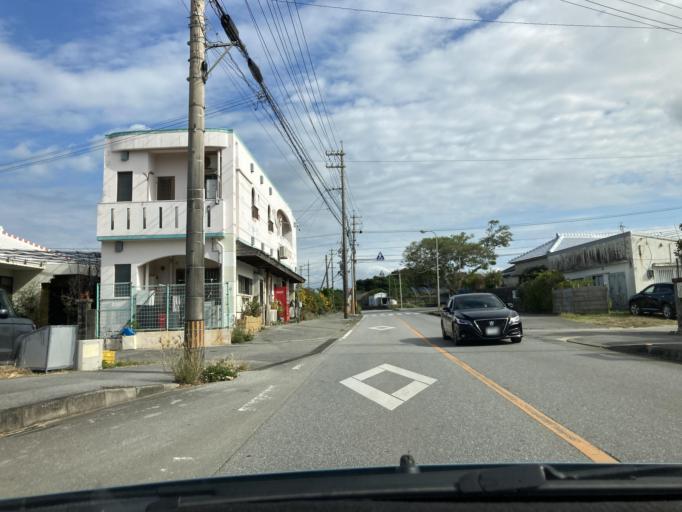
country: JP
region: Okinawa
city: Nago
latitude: 26.6916
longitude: 127.9593
